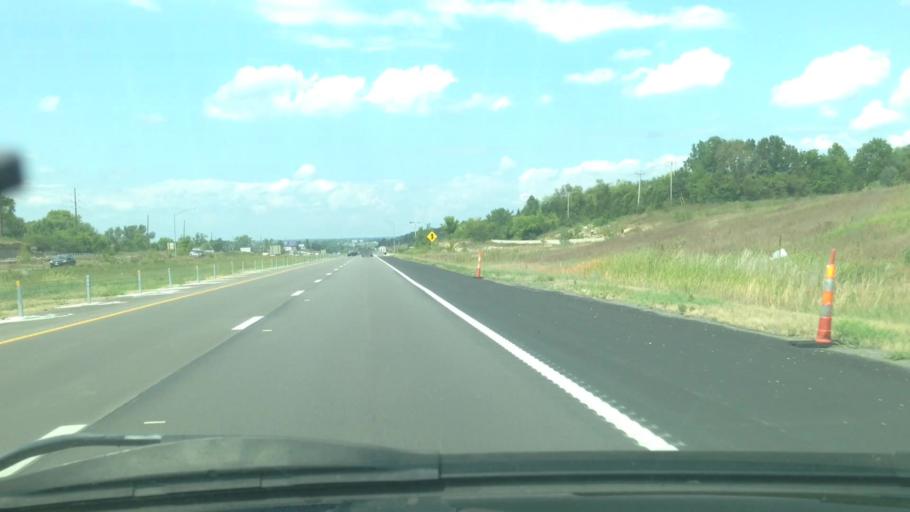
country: US
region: Missouri
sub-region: Lincoln County
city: Moscow Mills
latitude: 38.9088
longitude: -90.9234
